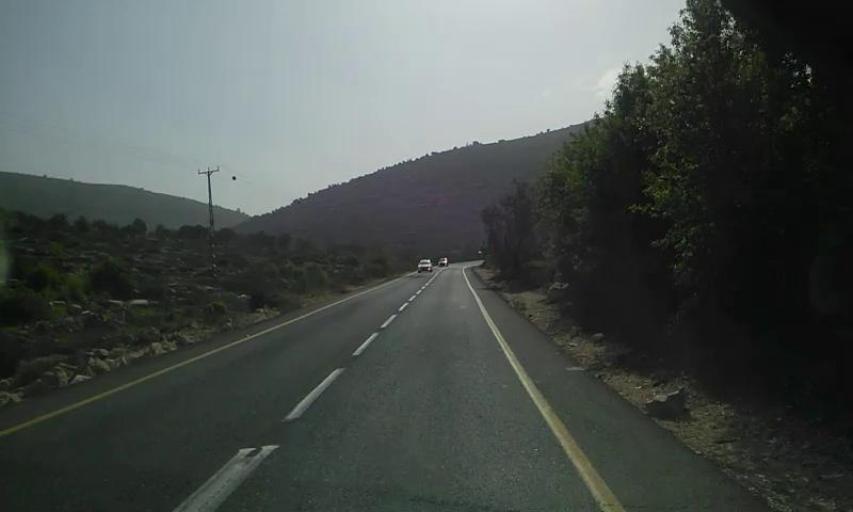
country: PS
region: West Bank
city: `Atarah
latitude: 31.9991
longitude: 35.2317
